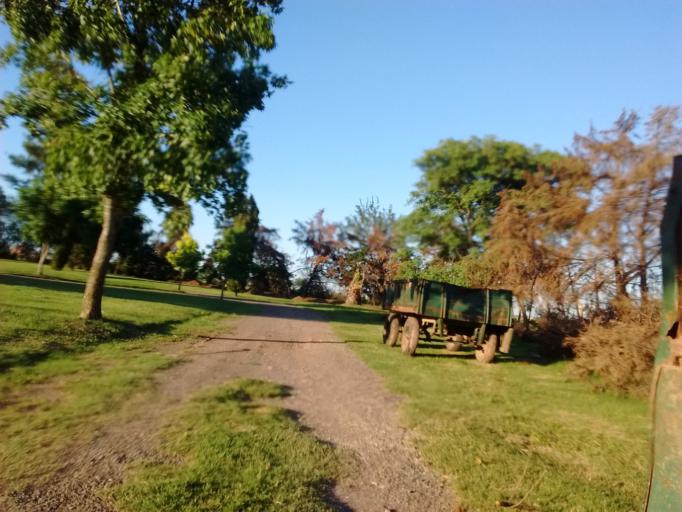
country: AR
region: Santa Fe
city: Funes
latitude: -32.9187
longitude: -60.7904
